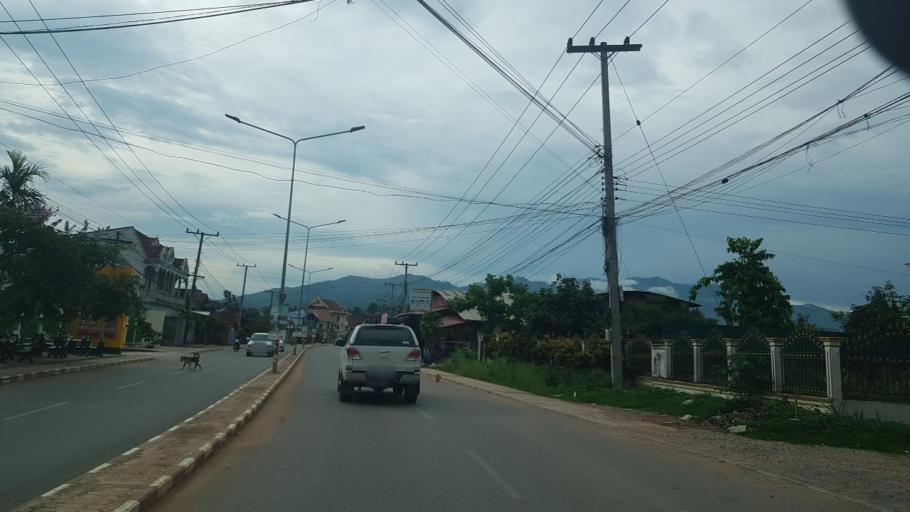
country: LA
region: Oudomxai
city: Muang Xay
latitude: 20.6784
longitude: 101.9870
